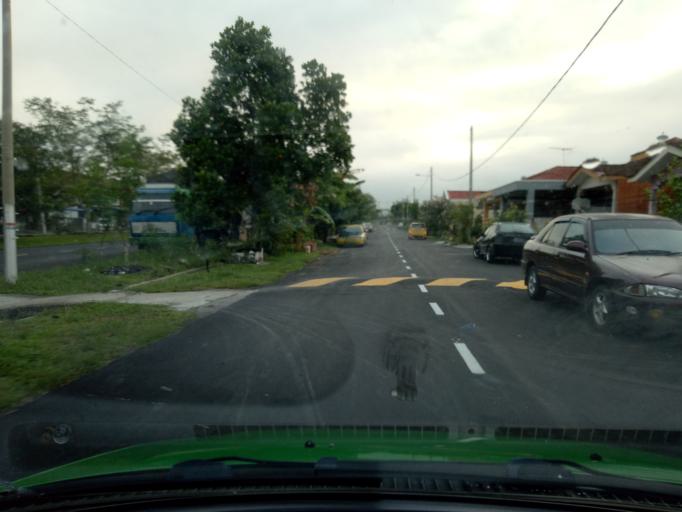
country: MY
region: Selangor
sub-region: Hulu Langat
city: Semenyih
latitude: 2.9293
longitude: 101.8591
